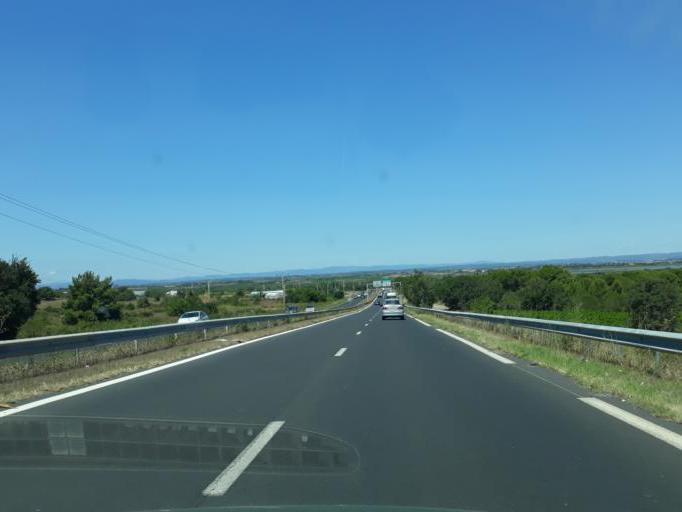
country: FR
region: Languedoc-Roussillon
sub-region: Departement de l'Herault
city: Le Cap d'Agde
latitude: 43.3003
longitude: 3.5077
